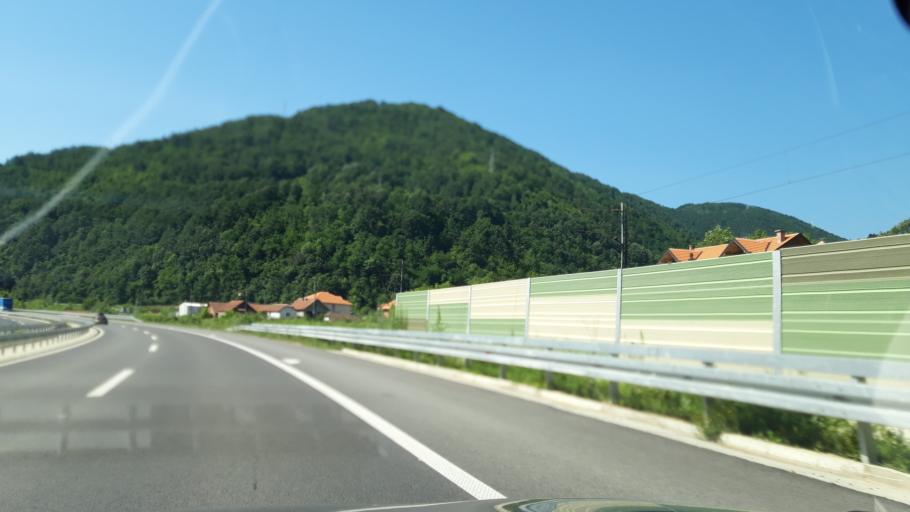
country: RS
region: Central Serbia
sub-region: Jablanicki Okrug
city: Vlasotince
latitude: 42.8613
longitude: 22.1194
